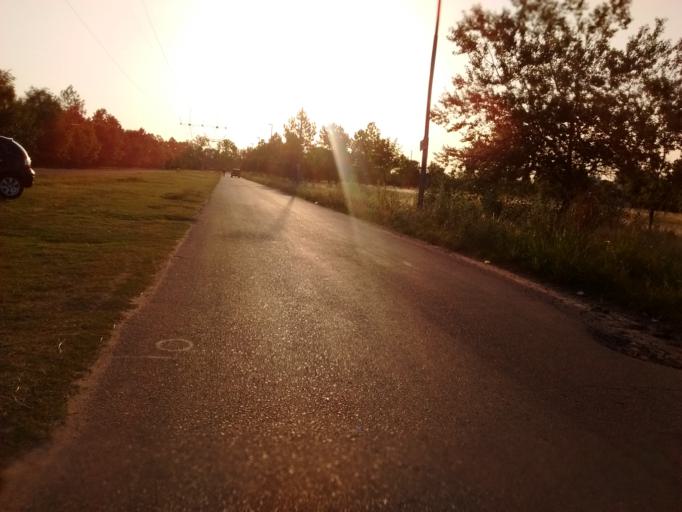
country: AR
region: Santa Fe
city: Funes
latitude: -32.9175
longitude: -60.7605
